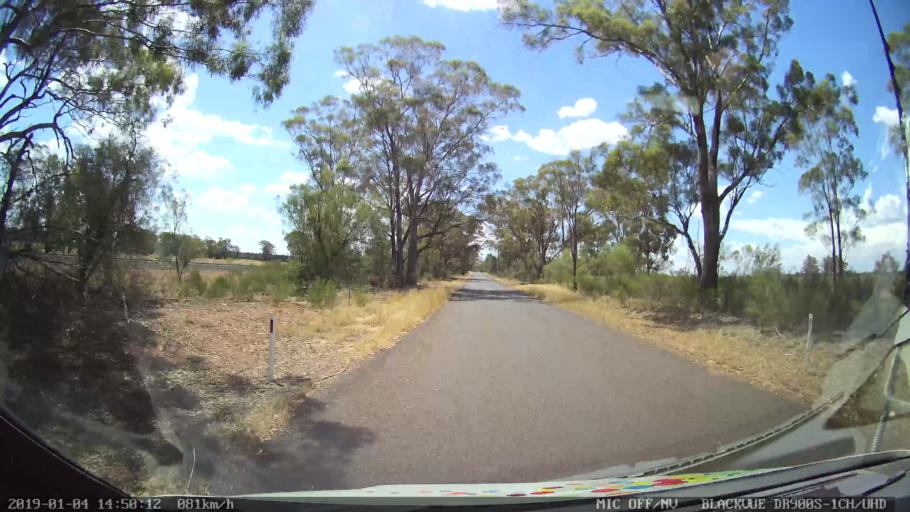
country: AU
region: New South Wales
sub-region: Dubbo Municipality
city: Dubbo
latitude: -32.0406
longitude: 148.6589
